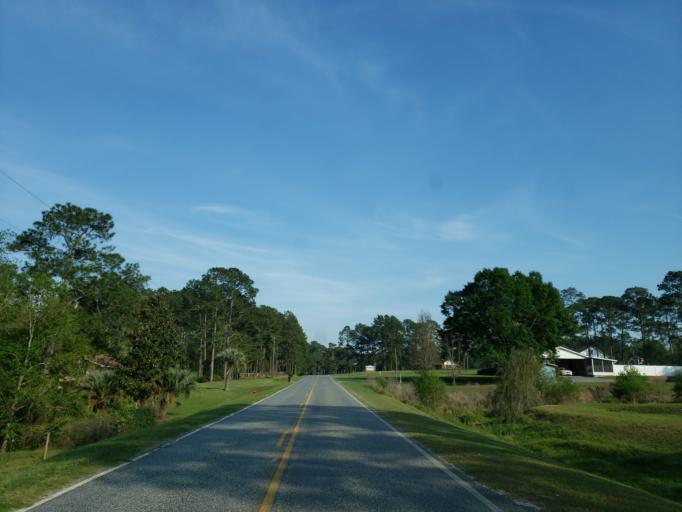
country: US
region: Georgia
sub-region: Tift County
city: Tifton
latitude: 31.4960
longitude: -83.5507
